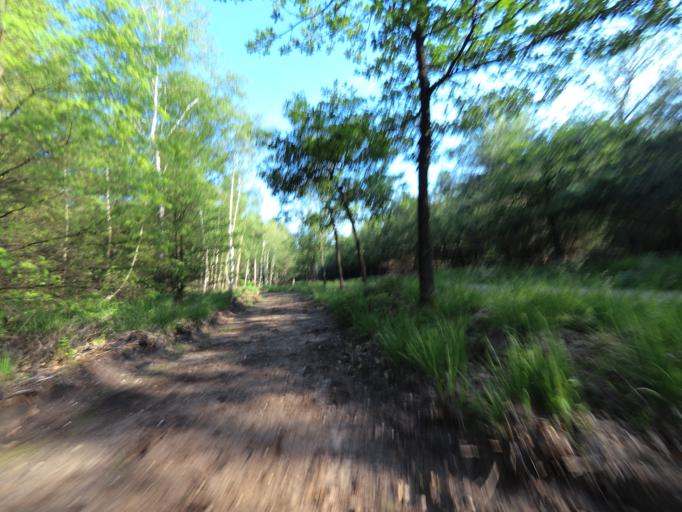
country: NL
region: Gelderland
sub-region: Gemeente Apeldoorn
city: Beekbergen
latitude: 52.1581
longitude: 5.8827
